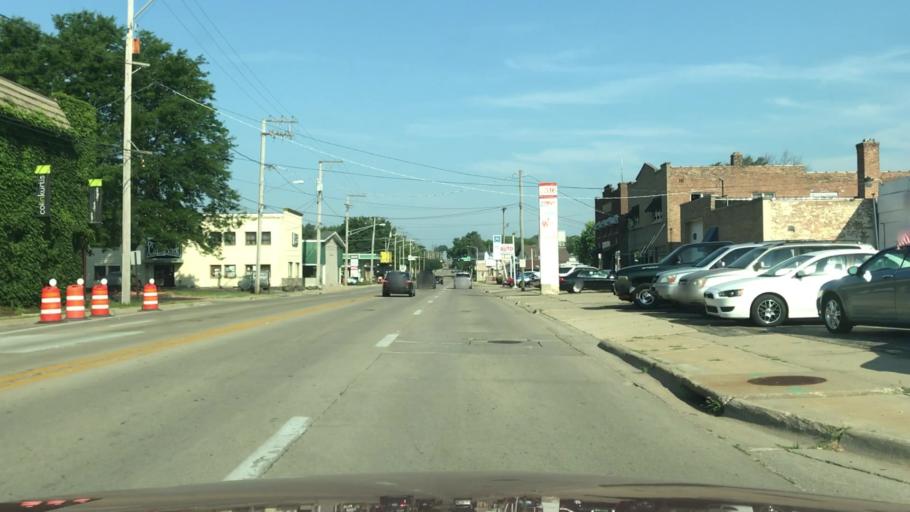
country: US
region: Illinois
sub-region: Winnebago County
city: Rockford
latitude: 42.2607
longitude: -89.0591
